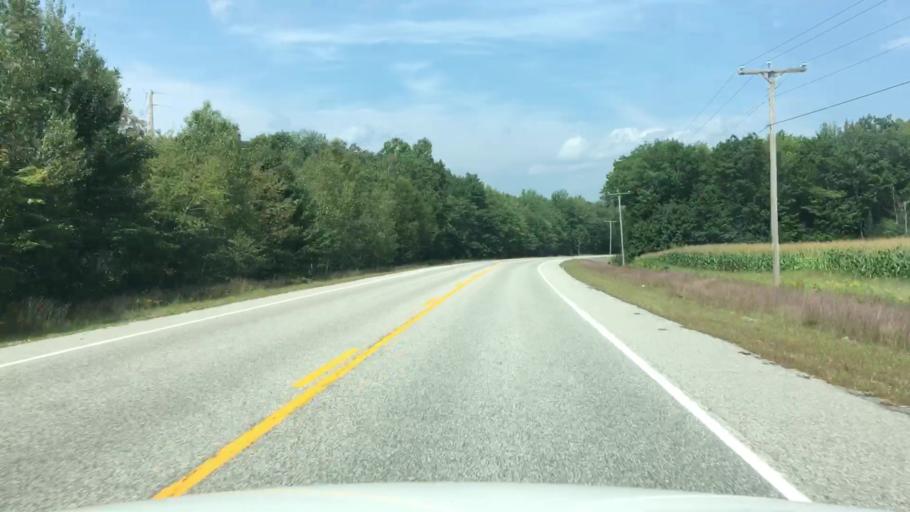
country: US
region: Maine
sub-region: Oxford County
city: Canton
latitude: 44.4718
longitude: -70.3255
